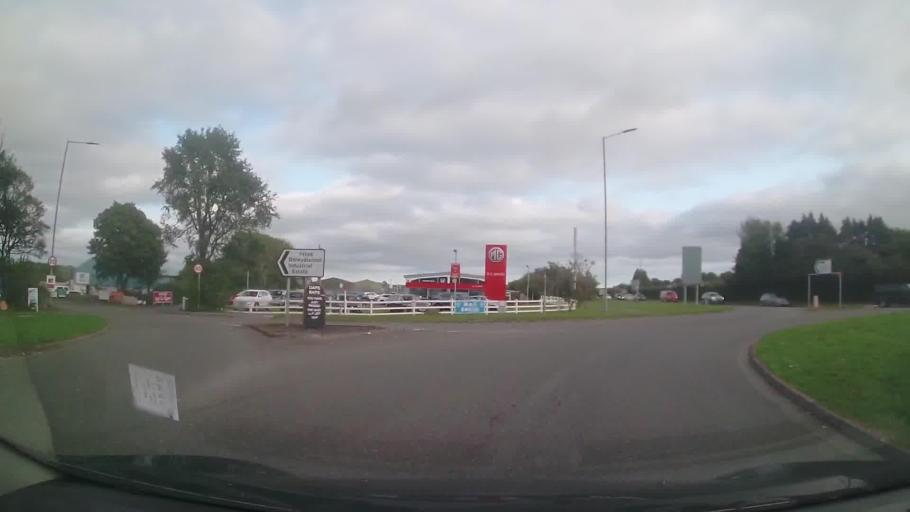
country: GB
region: Wales
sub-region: Pembrokeshire
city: Neyland
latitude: 51.7185
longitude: -4.9561
